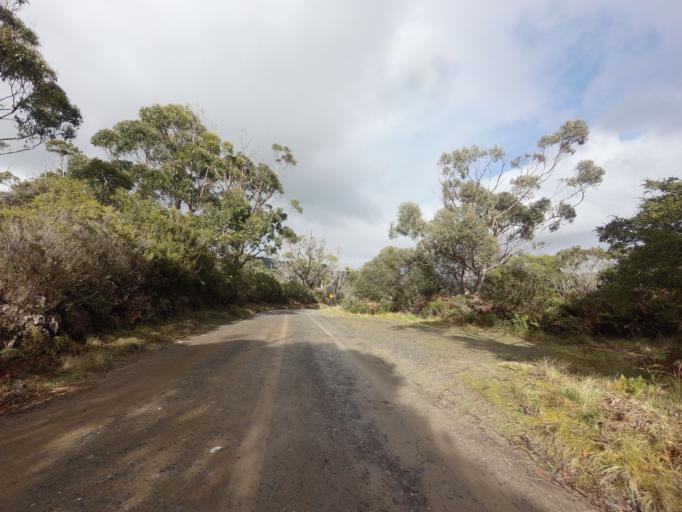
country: AU
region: Tasmania
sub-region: Huon Valley
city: Geeveston
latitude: -43.5802
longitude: 146.8988
